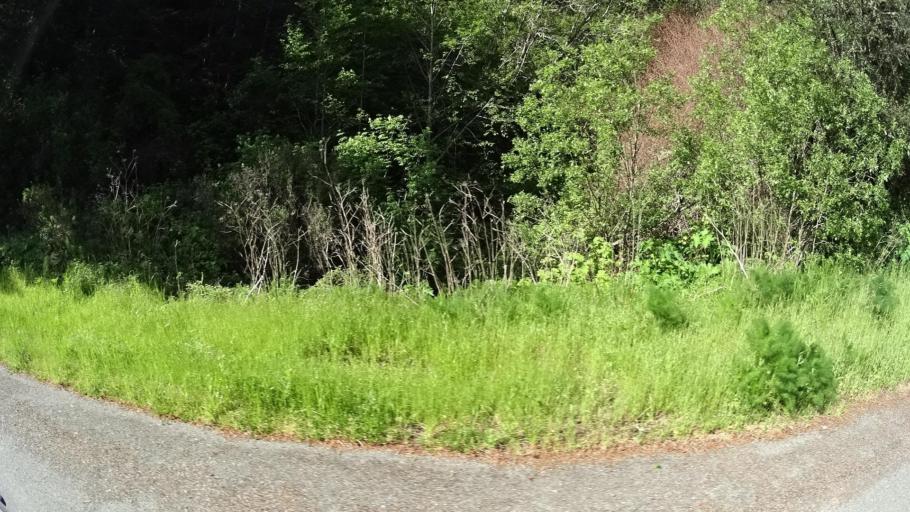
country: US
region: California
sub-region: Humboldt County
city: Ferndale
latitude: 40.3455
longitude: -124.3435
